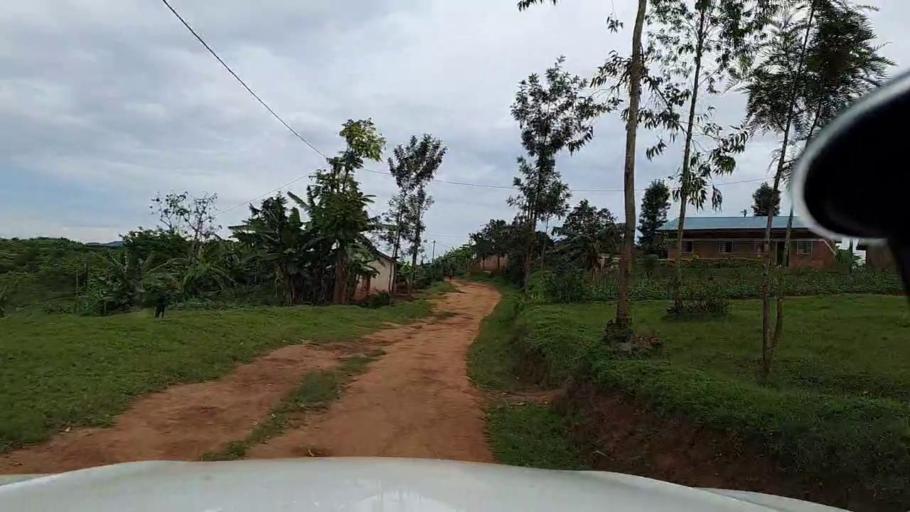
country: RW
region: Southern Province
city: Gitarama
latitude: -2.1159
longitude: 29.6404
